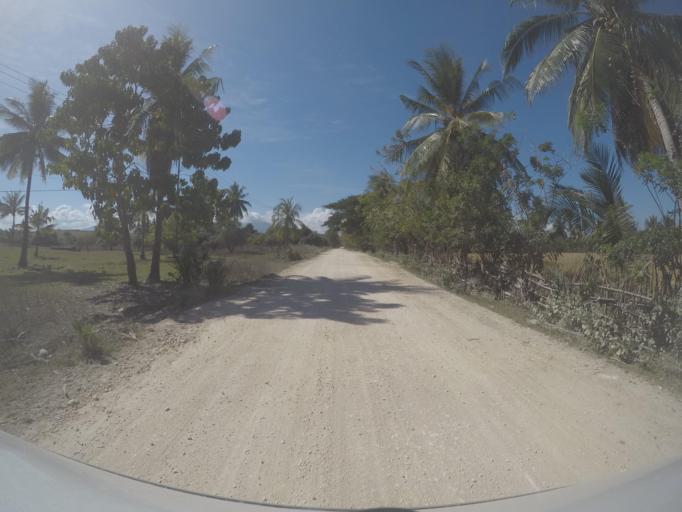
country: TL
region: Viqueque
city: Viqueque
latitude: -8.8797
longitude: 126.5075
